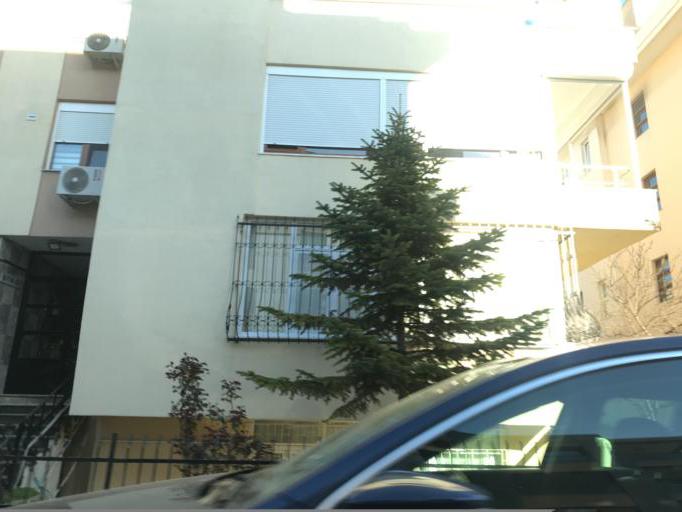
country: TR
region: Istanbul
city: Bahcelievler
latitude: 40.9618
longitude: 28.8294
